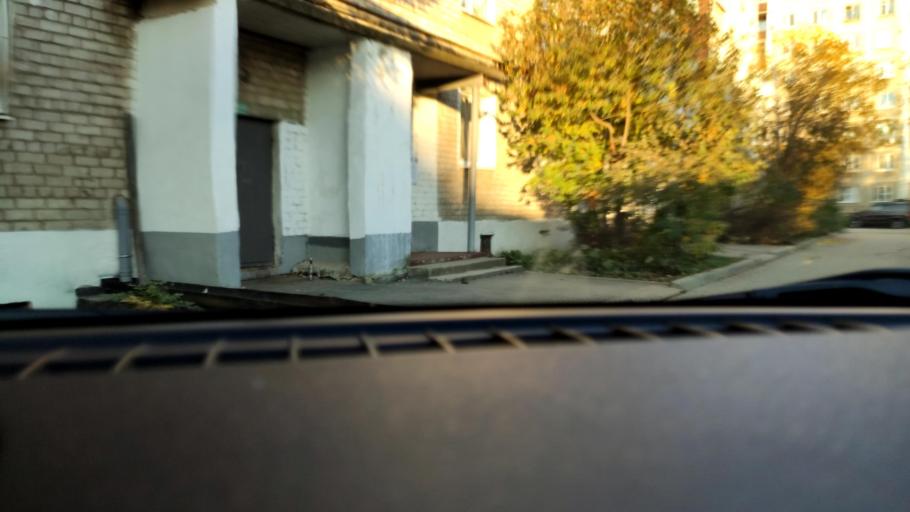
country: RU
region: Perm
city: Perm
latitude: 57.9695
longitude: 56.2691
